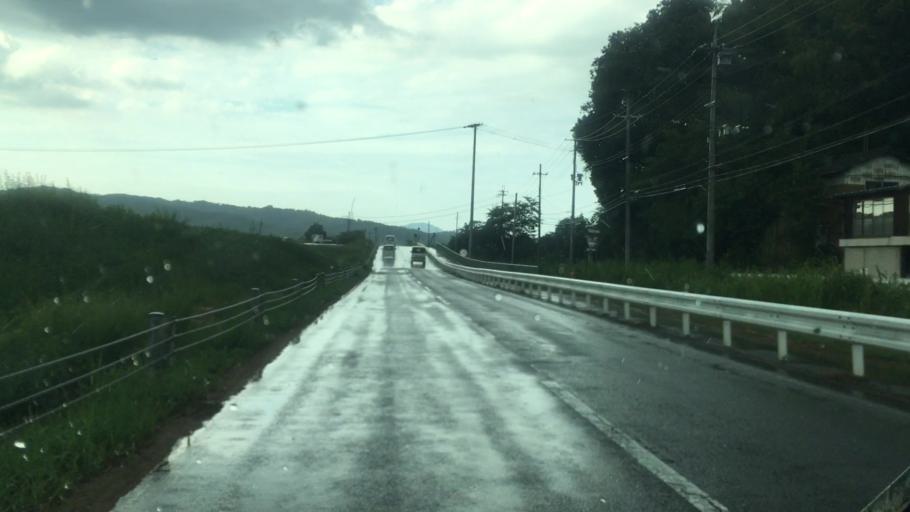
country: JP
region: Hyogo
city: Toyooka
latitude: 35.4872
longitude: 134.8169
